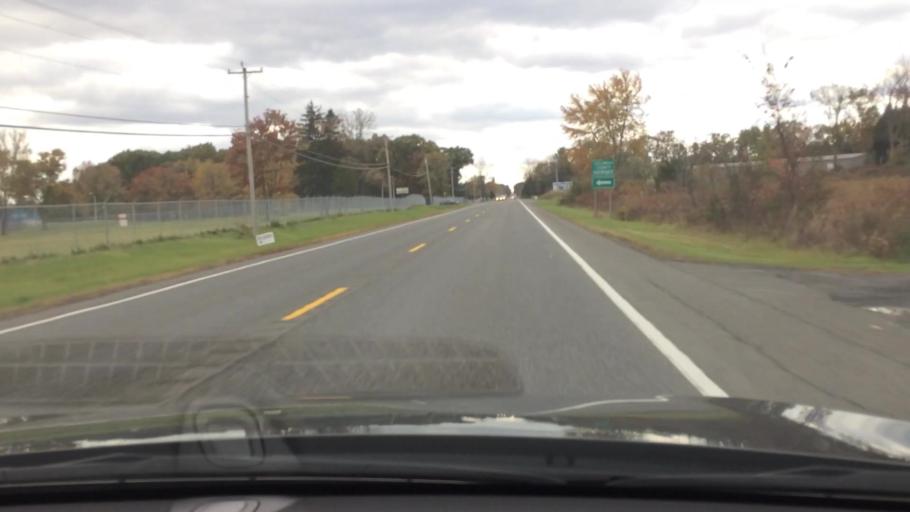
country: US
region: New York
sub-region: Columbia County
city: Stottville
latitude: 42.2964
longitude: -73.7131
